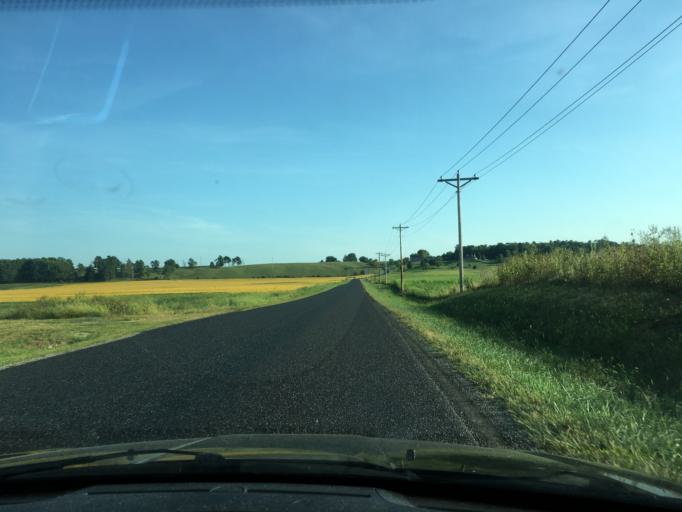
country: US
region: Ohio
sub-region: Logan County
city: West Liberty
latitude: 40.2787
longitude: -83.7250
